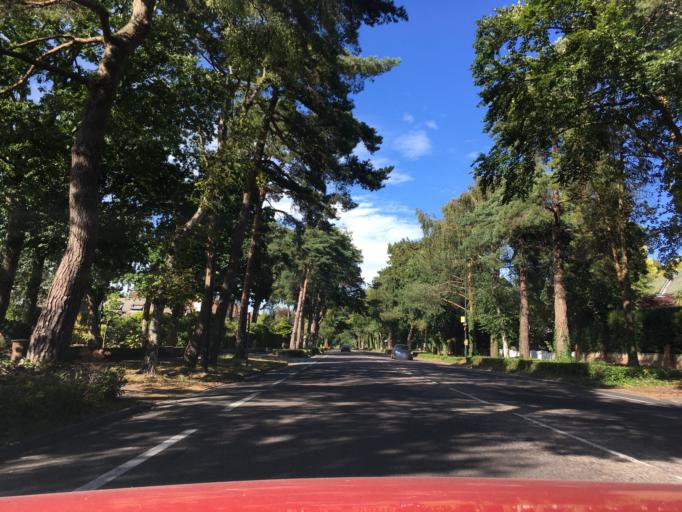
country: GB
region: England
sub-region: Bournemouth
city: Bournemouth
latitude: 50.7362
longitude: -1.8917
